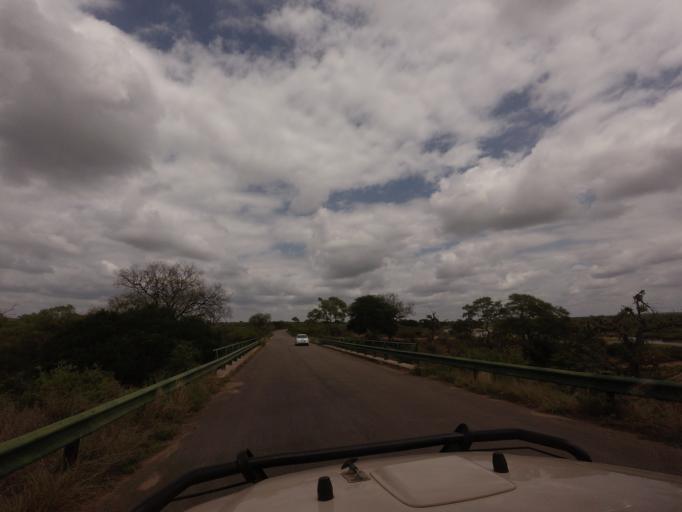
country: ZA
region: Mpumalanga
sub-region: Ehlanzeni District
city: Komatipoort
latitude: -25.1011
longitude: 31.8856
